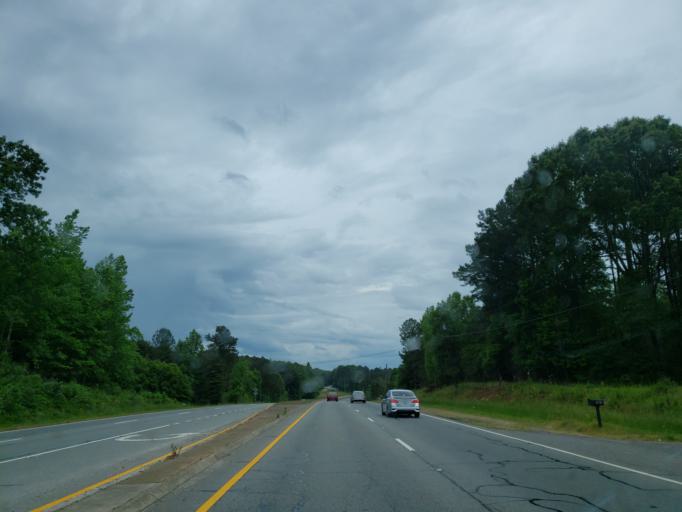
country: US
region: Georgia
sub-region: Haralson County
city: Bremen
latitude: 33.7585
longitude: -85.1625
